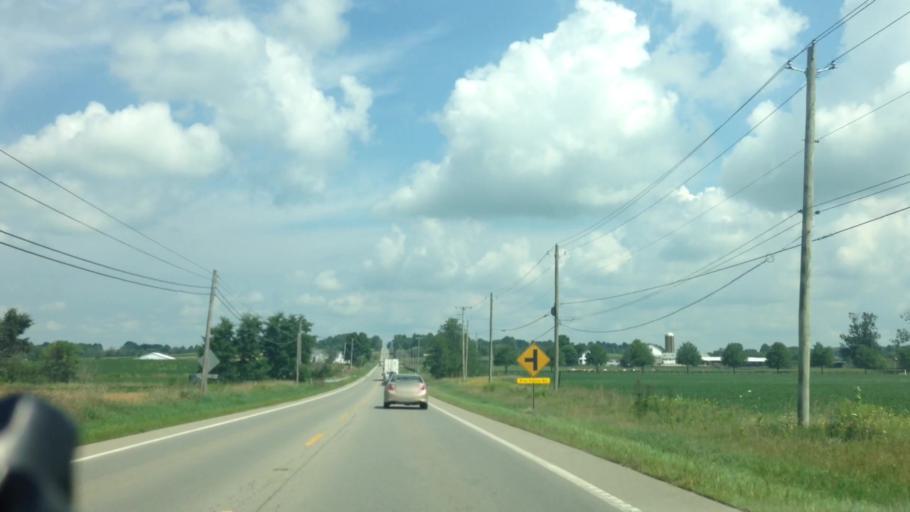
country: US
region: Ohio
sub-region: Wayne County
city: Orrville
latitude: 40.8709
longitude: -81.7634
